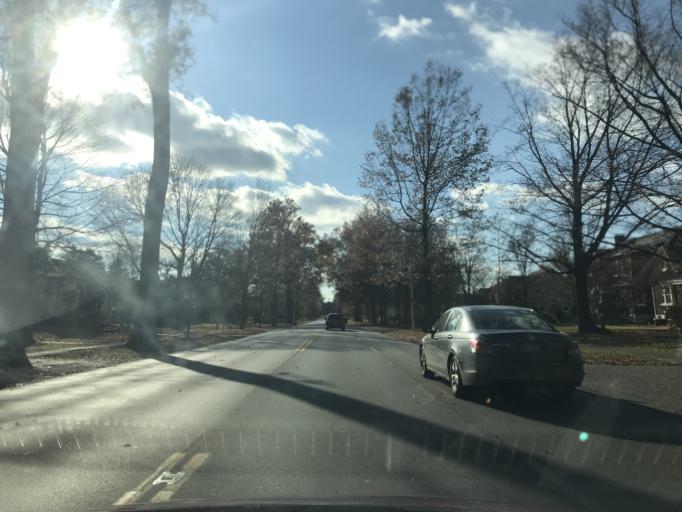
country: US
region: Kentucky
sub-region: Jefferson County
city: Audubon Park
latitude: 38.2180
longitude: -85.7368
